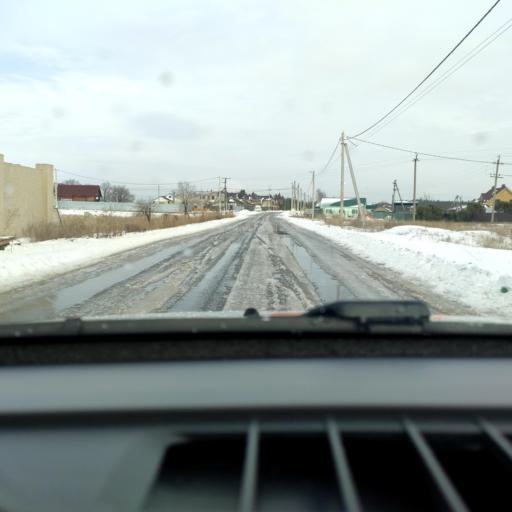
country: RU
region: Voronezj
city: Podgornoye
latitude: 51.7727
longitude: 39.1243
